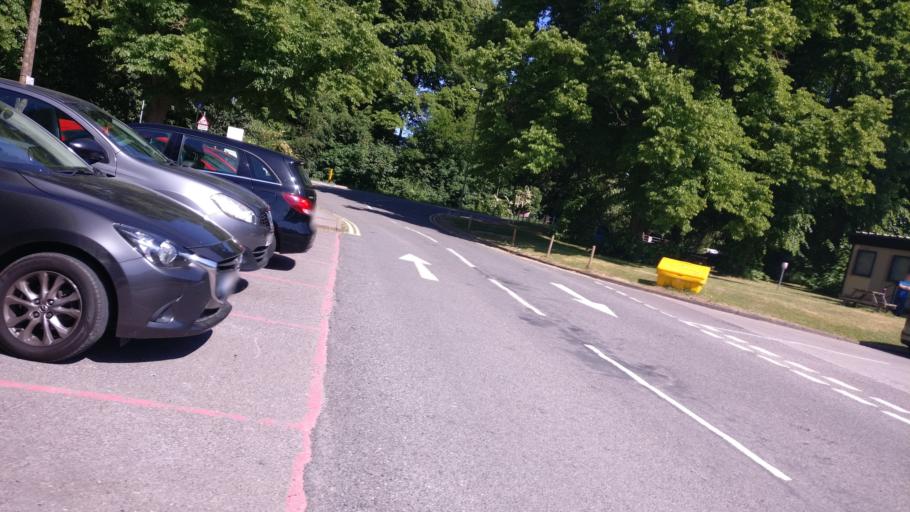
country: GB
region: England
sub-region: Hampshire
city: Basingstoke
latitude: 51.2811
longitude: -1.1121
